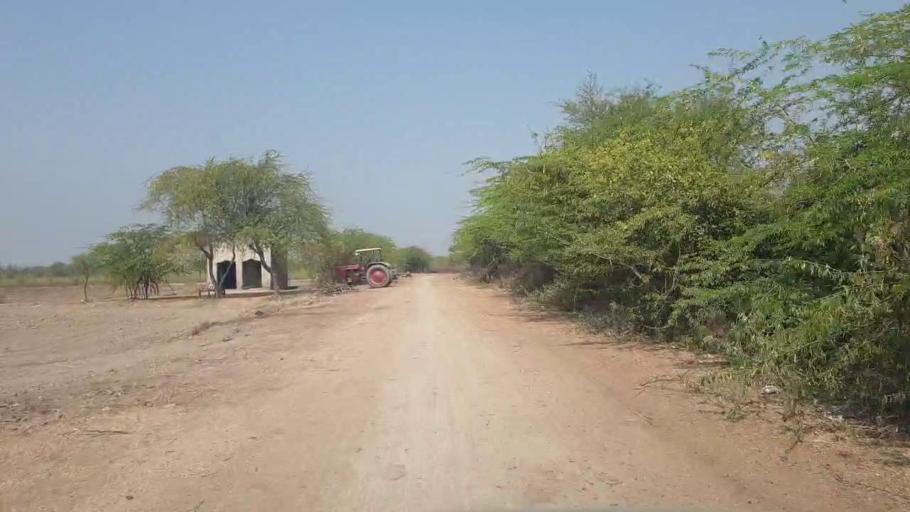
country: PK
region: Sindh
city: Umarkot
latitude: 25.4470
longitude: 69.6656
